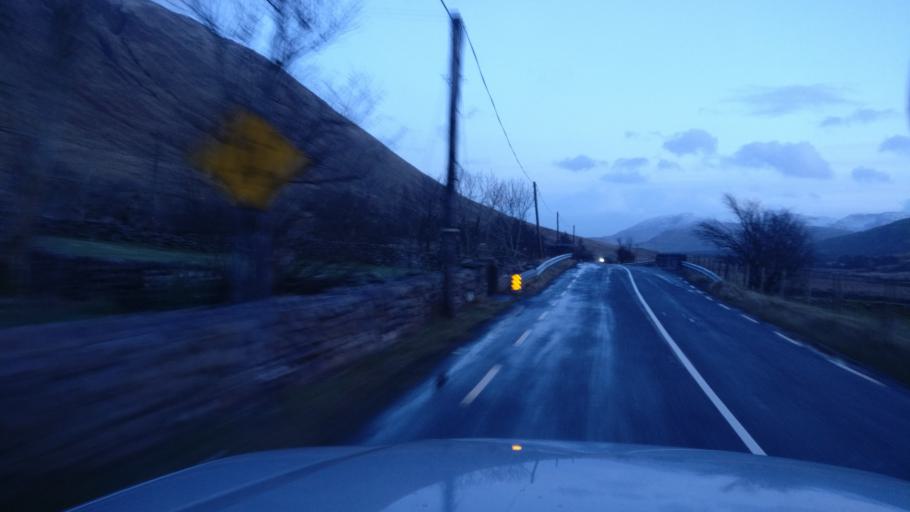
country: IE
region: Connaught
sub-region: Maigh Eo
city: Westport
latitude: 53.5705
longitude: -9.6570
